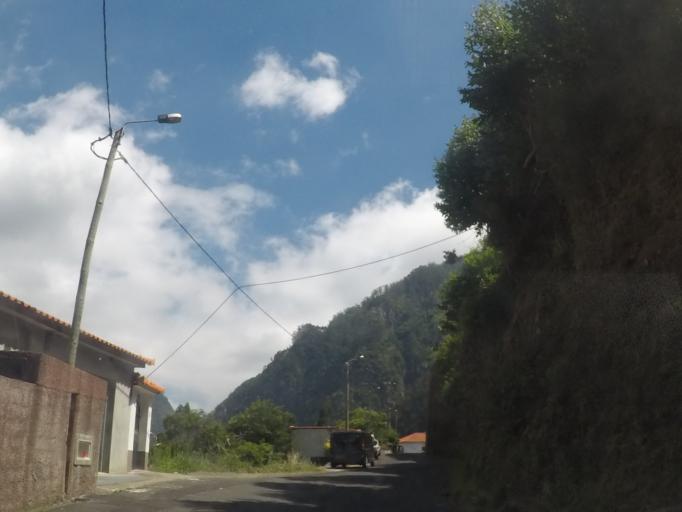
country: PT
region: Madeira
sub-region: Camara de Lobos
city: Curral das Freiras
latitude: 32.7099
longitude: -16.9732
